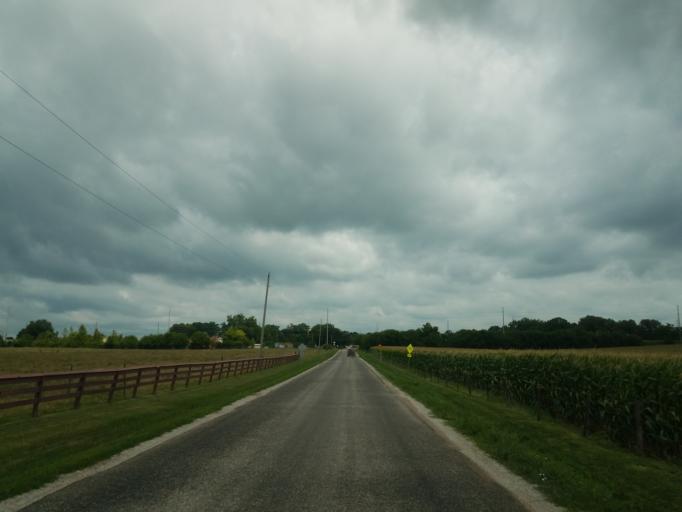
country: US
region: Illinois
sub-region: McLean County
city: Bloomington
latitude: 40.4767
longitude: -89.0329
